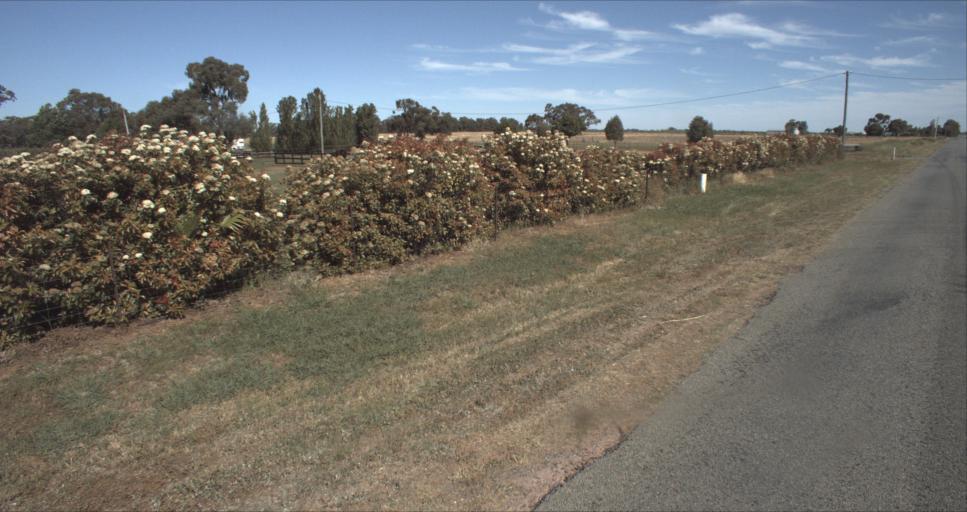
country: AU
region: New South Wales
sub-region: Leeton
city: Leeton
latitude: -34.5594
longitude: 146.3839
